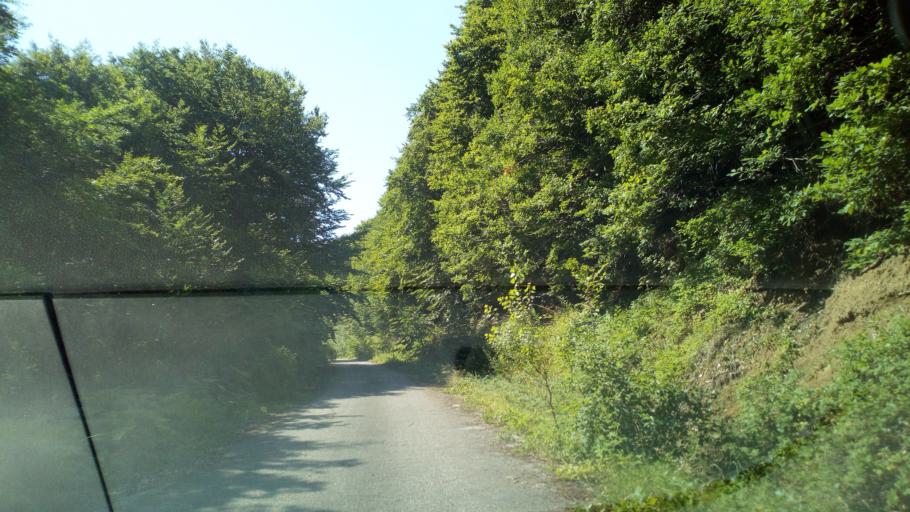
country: GR
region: Central Macedonia
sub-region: Nomos Thessalonikis
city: Sochos
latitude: 40.8281
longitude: 23.3562
